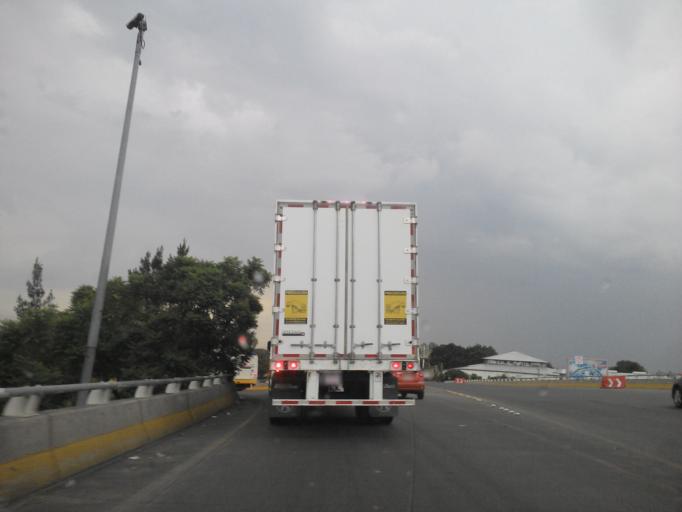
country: MX
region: Jalisco
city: Tlaquepaque
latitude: 20.6293
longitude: -103.2939
